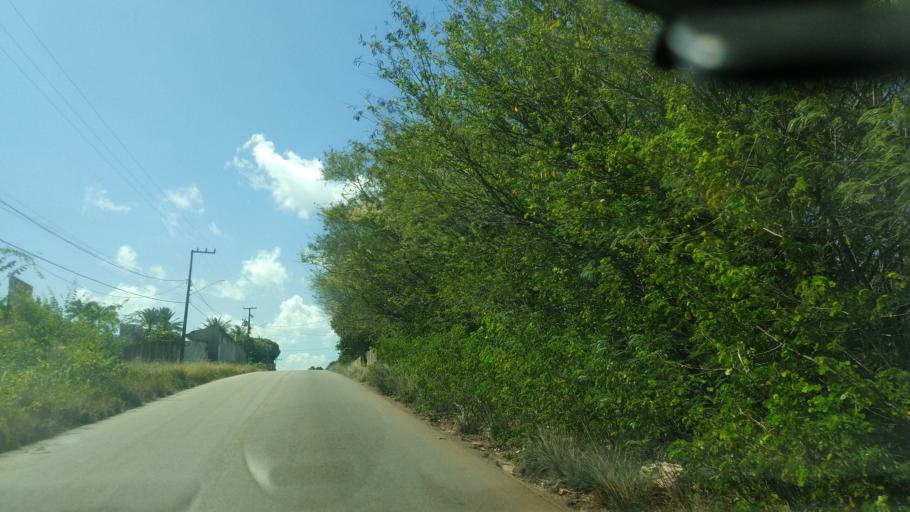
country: BR
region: Rio Grande do Norte
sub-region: Parnamirim
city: Parnamirim
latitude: -5.9501
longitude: -35.1788
